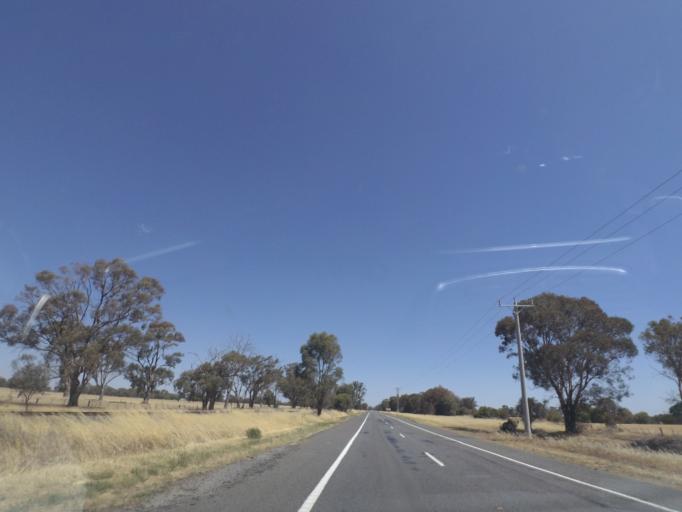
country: AU
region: Victoria
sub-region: Greater Shepparton
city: Shepparton
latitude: -36.2123
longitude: 145.4319
